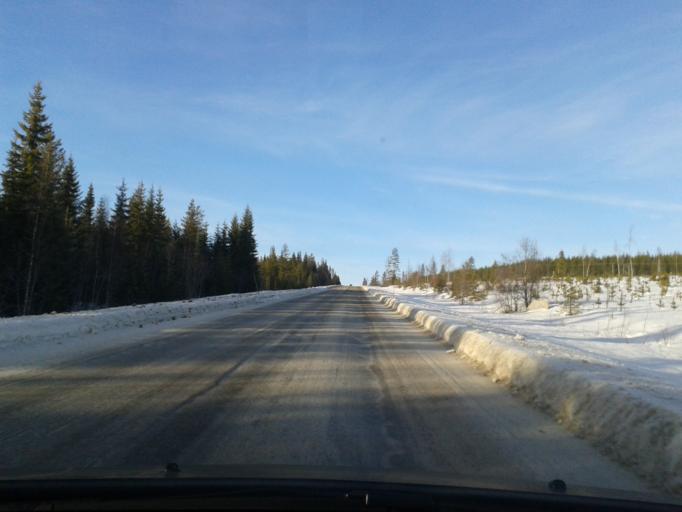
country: SE
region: Vaesternorrland
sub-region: OErnskoeldsviks Kommun
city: Bredbyn
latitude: 63.7641
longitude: 17.6873
